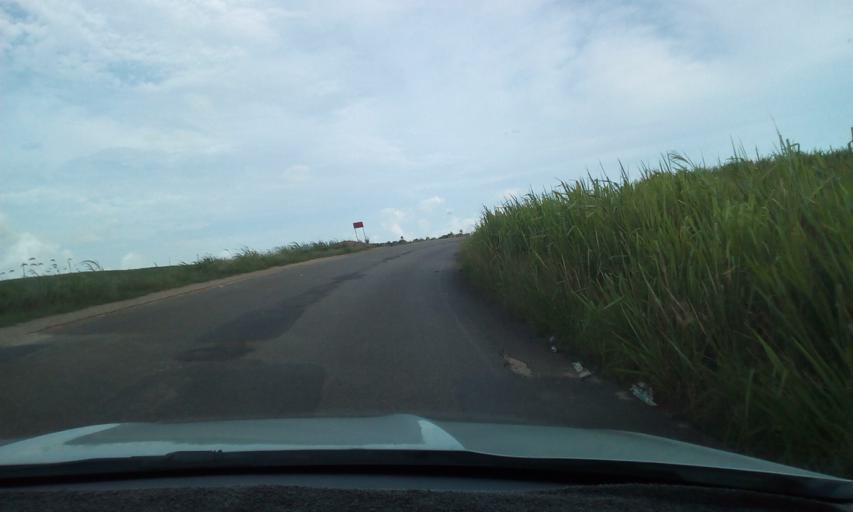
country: BR
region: Pernambuco
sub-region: Gloria Do Goita
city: Gloria do Goita
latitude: -7.9904
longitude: -35.2311
